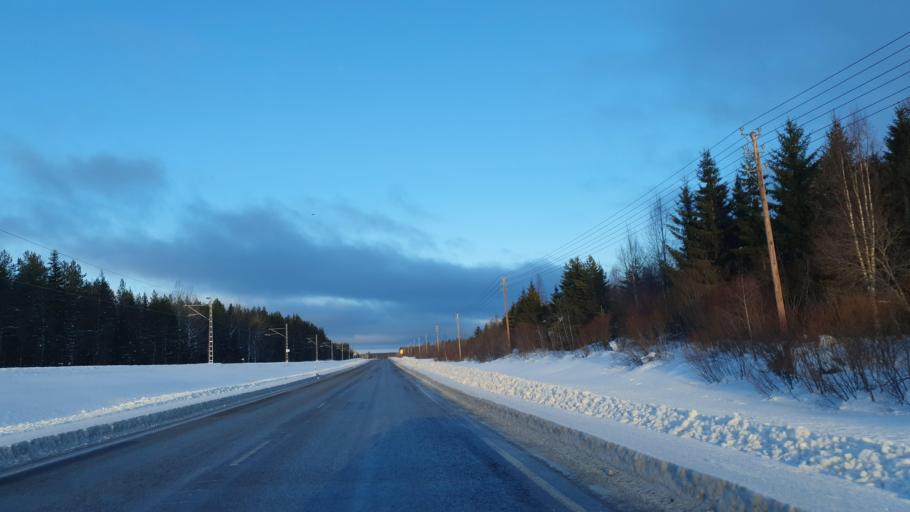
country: FI
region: Kainuu
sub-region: Kajaani
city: Paltamo
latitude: 64.4099
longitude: 27.7577
